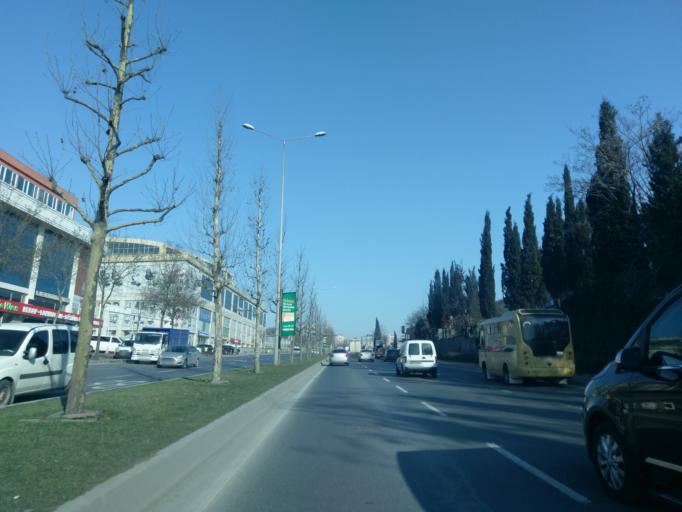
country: TR
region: Istanbul
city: Basaksehir
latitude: 41.0924
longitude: 28.7943
